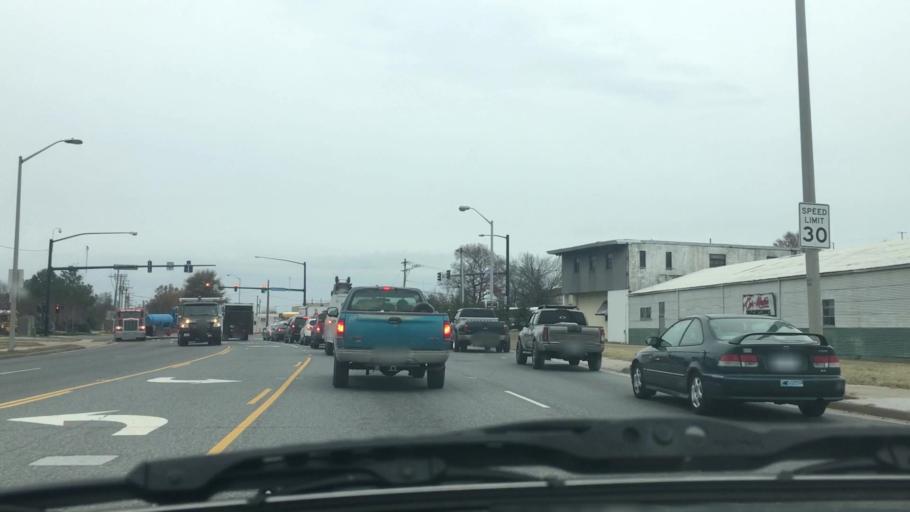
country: US
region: Virginia
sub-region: City of Norfolk
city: Norfolk
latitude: 36.8521
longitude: -76.2480
